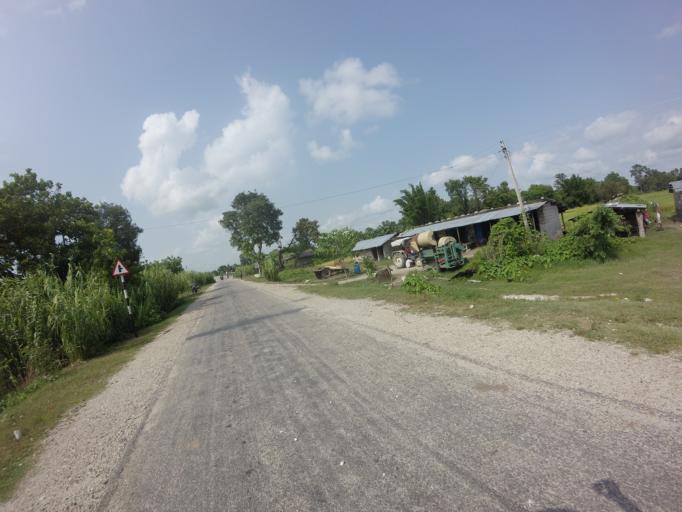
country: NP
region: Far Western
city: Tikapur
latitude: 28.4669
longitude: 81.0752
